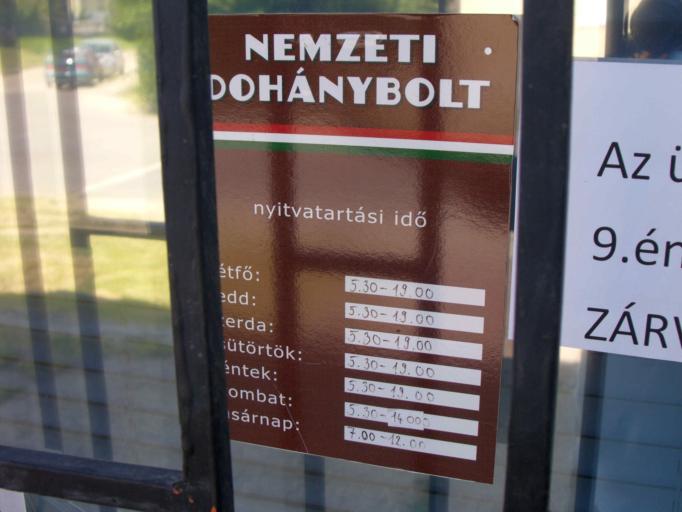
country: HU
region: Komarom-Esztergom
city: Labatlan
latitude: 47.7474
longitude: 18.4978
